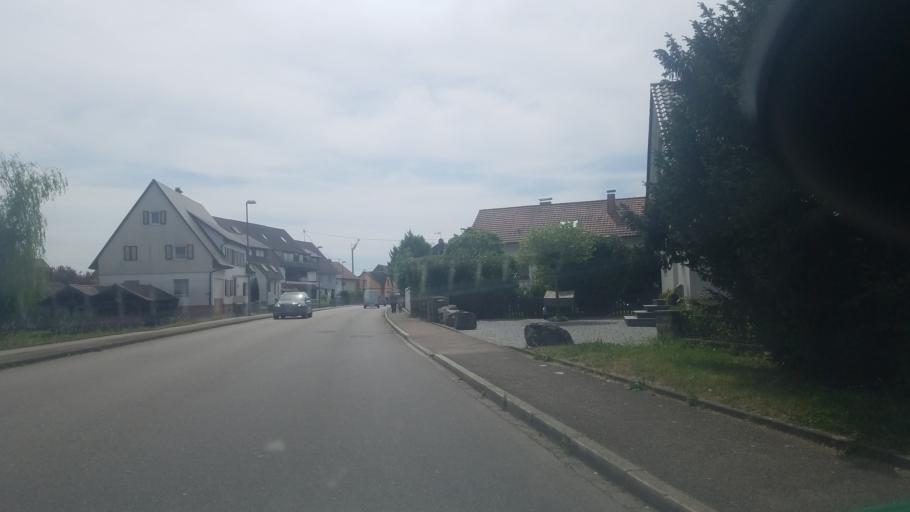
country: DE
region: Baden-Wuerttemberg
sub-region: Freiburg Region
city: Meissenheim
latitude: 48.4373
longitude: 7.8129
